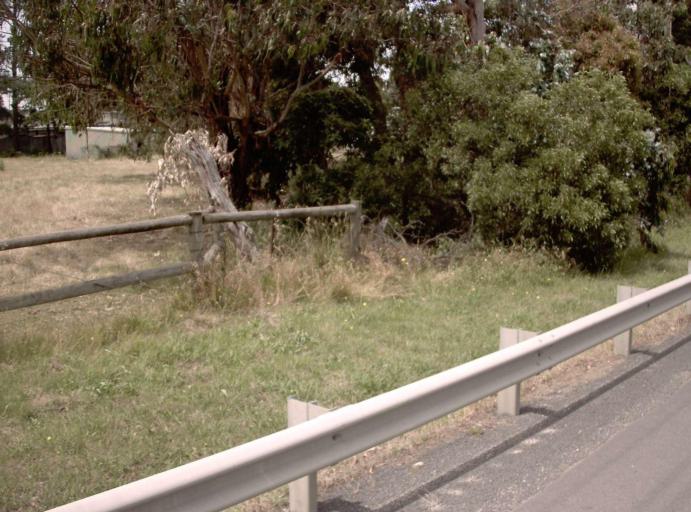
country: AU
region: Victoria
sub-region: Mornington Peninsula
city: Tyabb
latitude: -38.2701
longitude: 145.1928
